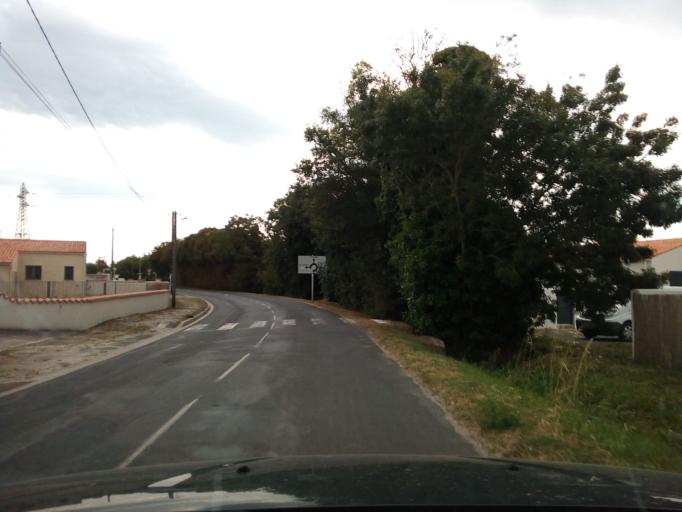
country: FR
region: Poitou-Charentes
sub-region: Departement de la Charente-Maritime
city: Dolus-d'Oleron
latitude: 45.9264
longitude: -1.3201
